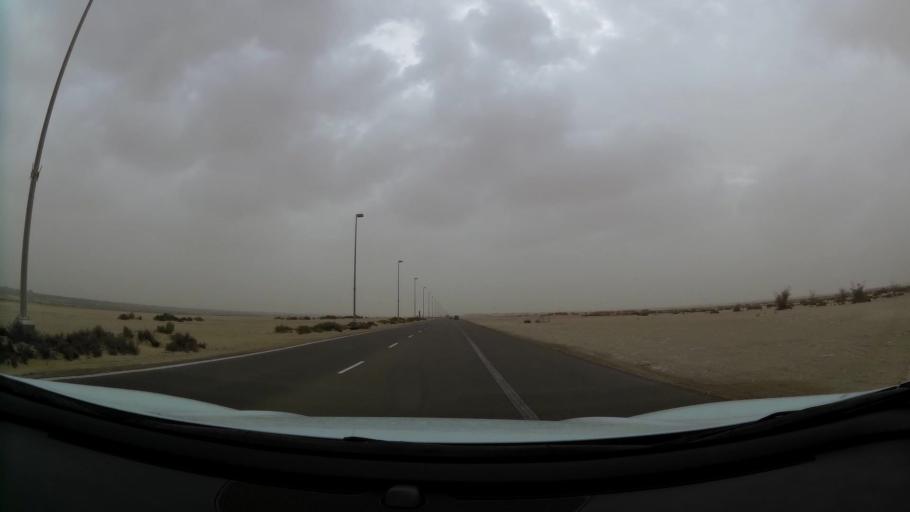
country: AE
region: Abu Dhabi
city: Abu Dhabi
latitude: 24.4612
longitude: 54.6968
